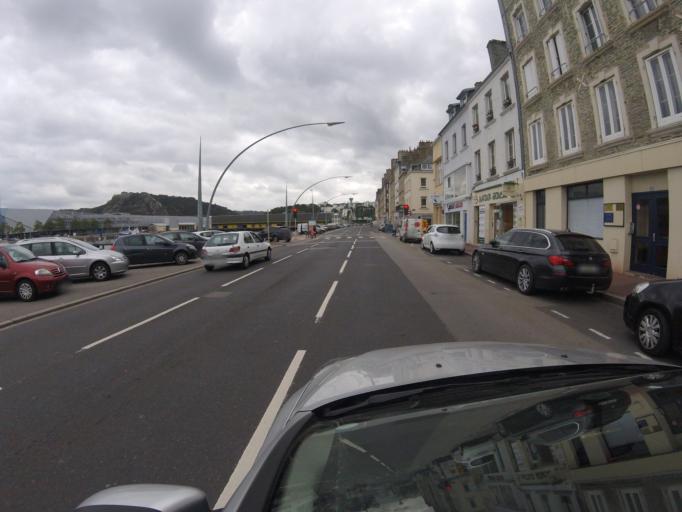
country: FR
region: Lower Normandy
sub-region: Departement de la Manche
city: Cherbourg-Octeville
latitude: 49.6373
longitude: -1.6217
